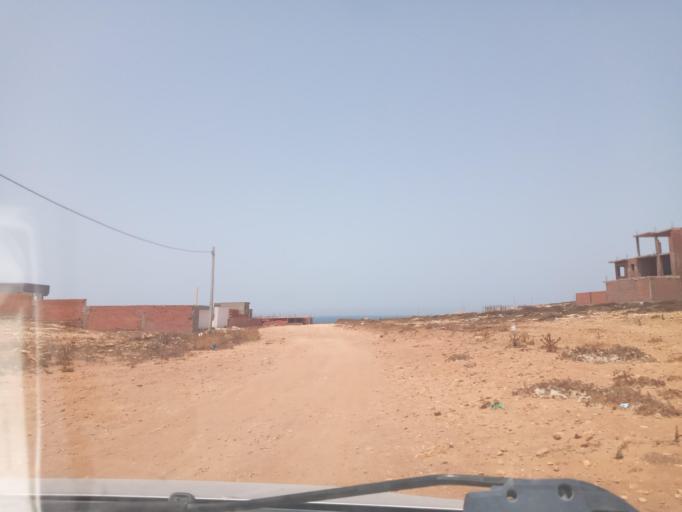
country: TN
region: Nabul
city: El Haouaria
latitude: 37.0534
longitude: 11.0000
